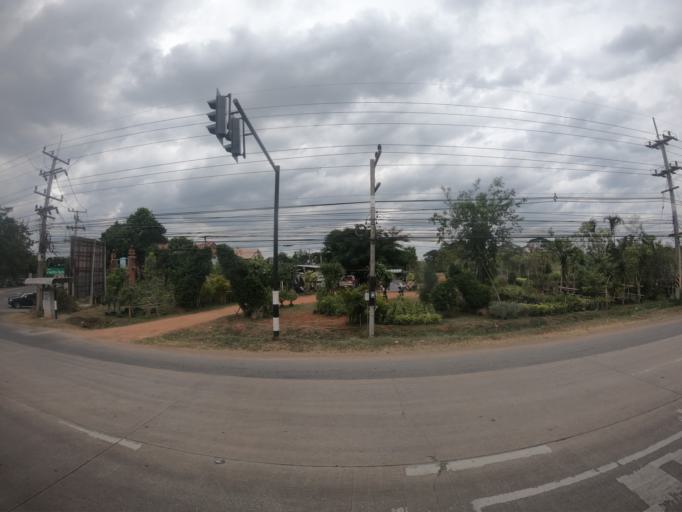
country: TH
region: Nakhon Ratchasima
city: Nakhon Ratchasima
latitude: 14.8658
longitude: 102.1844
